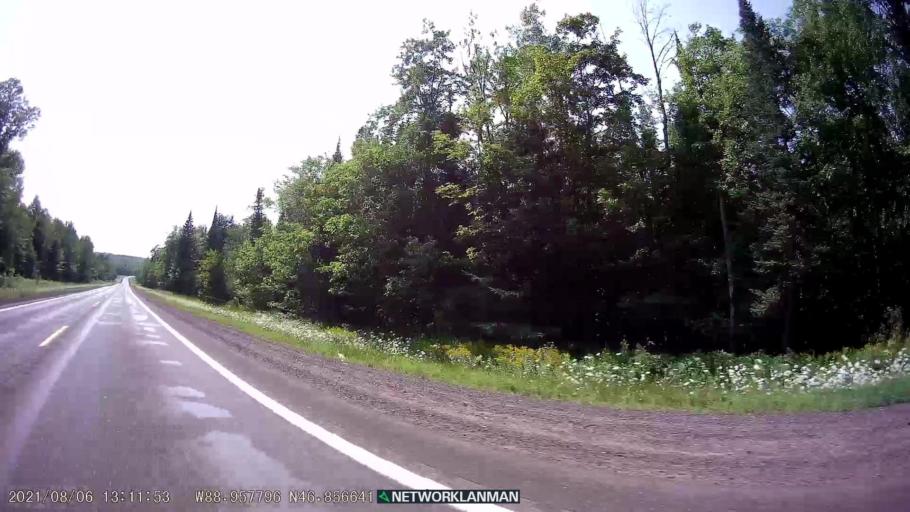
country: US
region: Michigan
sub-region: Ontonagon County
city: Ontonagon
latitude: 46.8565
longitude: -88.9578
